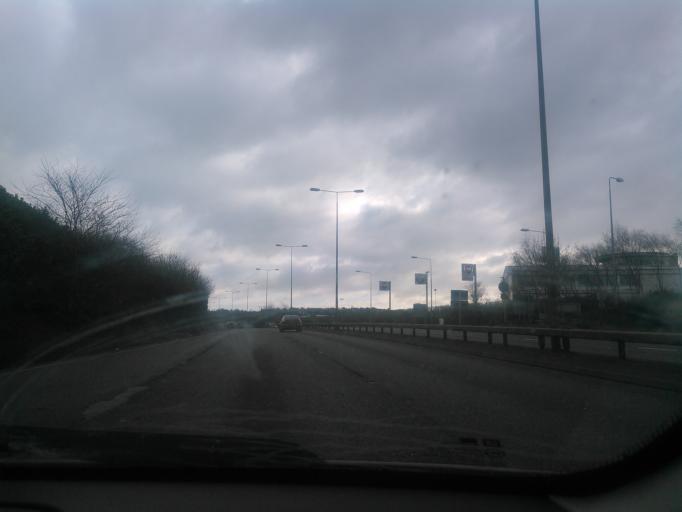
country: GB
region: England
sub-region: Staffordshire
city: Longton
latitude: 52.9841
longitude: -2.1320
